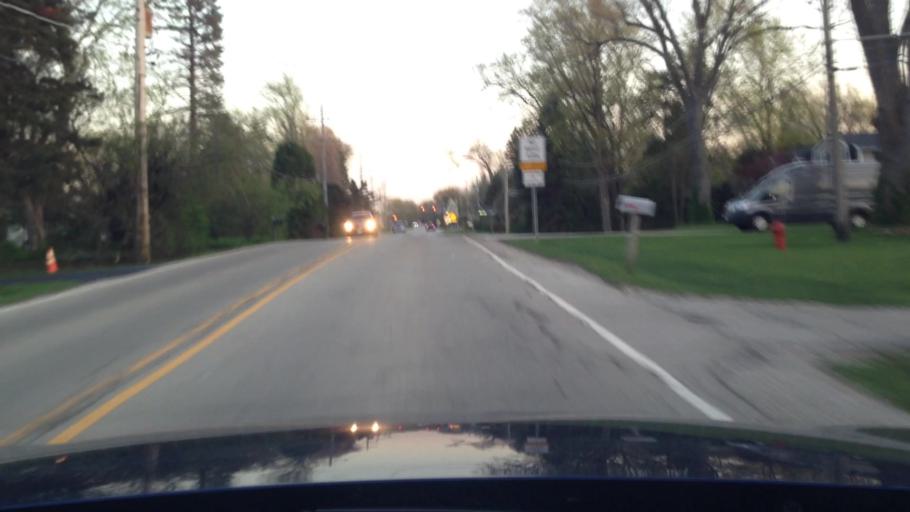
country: US
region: Illinois
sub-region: Cook County
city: Prospect Heights
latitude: 42.0982
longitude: -87.9272
